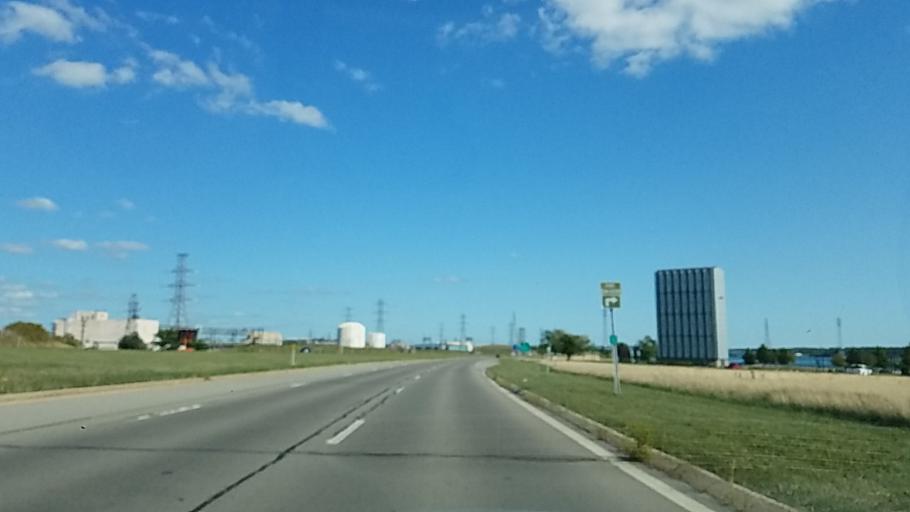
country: US
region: New York
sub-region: Niagara County
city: Niagara Falls
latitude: 43.0783
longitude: -79.0171
